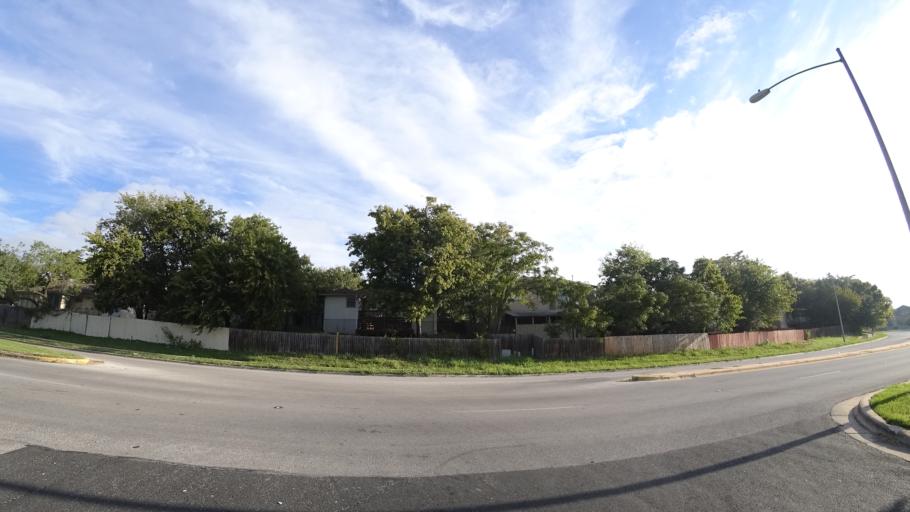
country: US
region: Texas
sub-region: Travis County
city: Onion Creek
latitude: 30.1908
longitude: -97.7341
